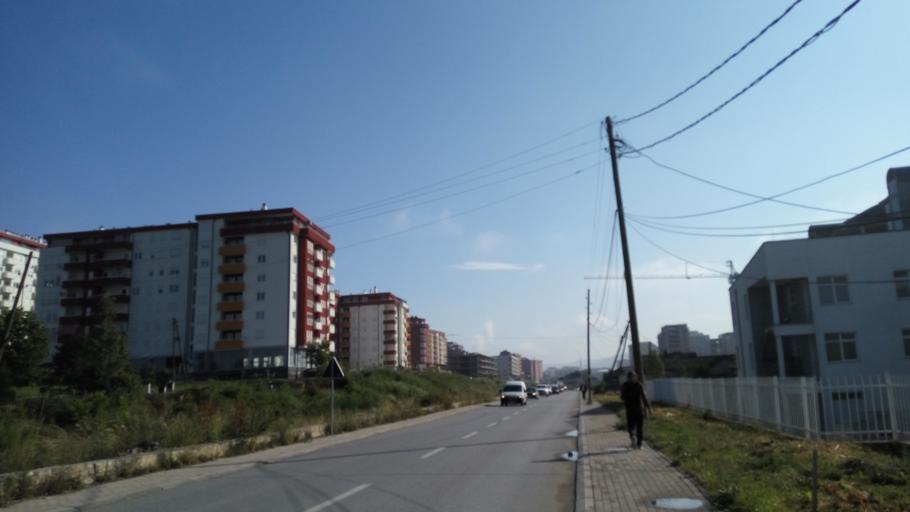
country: XK
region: Pristina
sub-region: Komuna e Prishtines
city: Pristina
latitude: 42.6545
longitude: 21.1466
